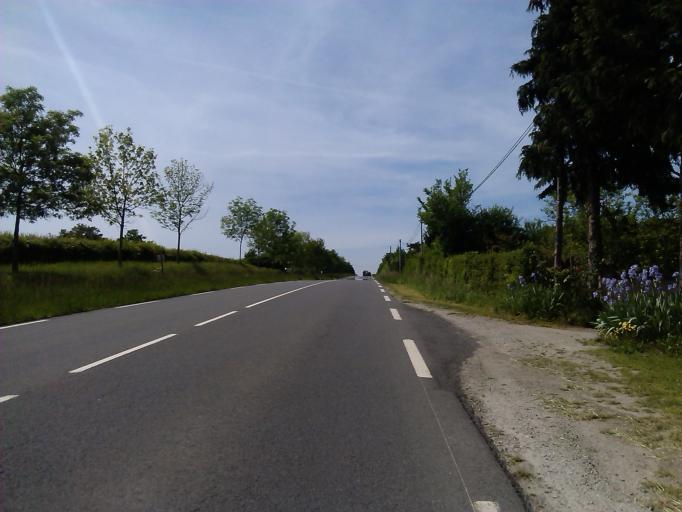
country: FR
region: Auvergne
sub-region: Departement de l'Allier
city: Souvigny
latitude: 46.5885
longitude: 3.1428
